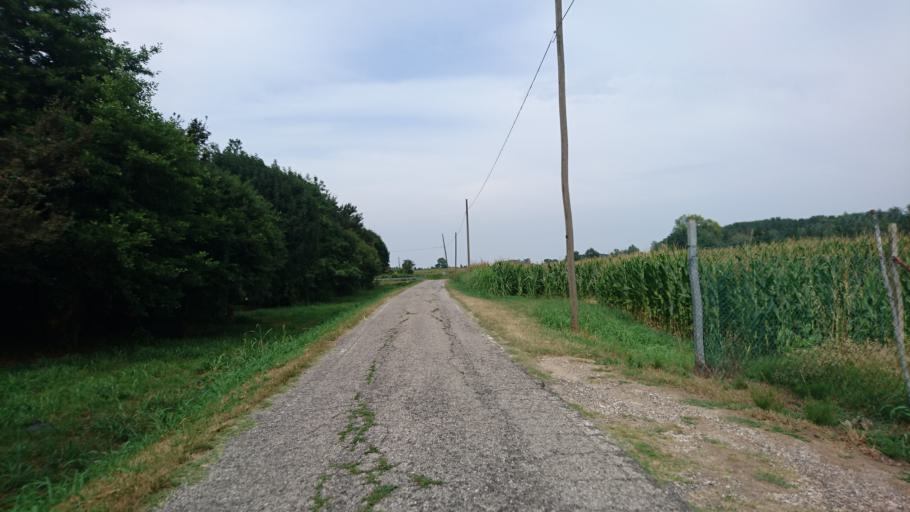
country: IT
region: Veneto
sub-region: Provincia di Venezia
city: Sant'Anna
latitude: 45.1451
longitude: 12.3002
